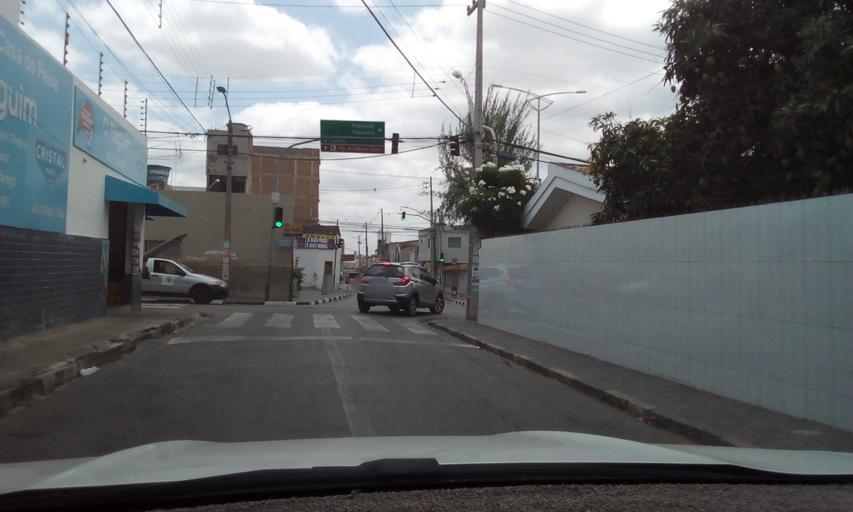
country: BR
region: Pernambuco
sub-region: Caruaru
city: Caruaru
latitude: -8.2890
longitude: -35.9793
